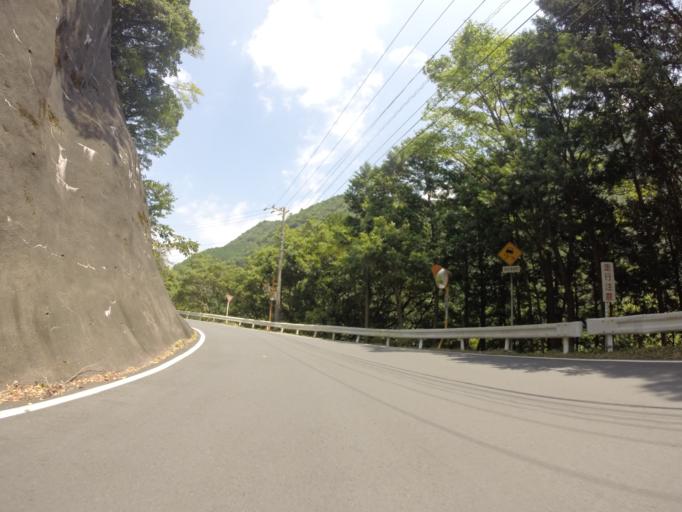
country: JP
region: Shizuoka
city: Shizuoka-shi
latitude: 35.2301
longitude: 138.3471
